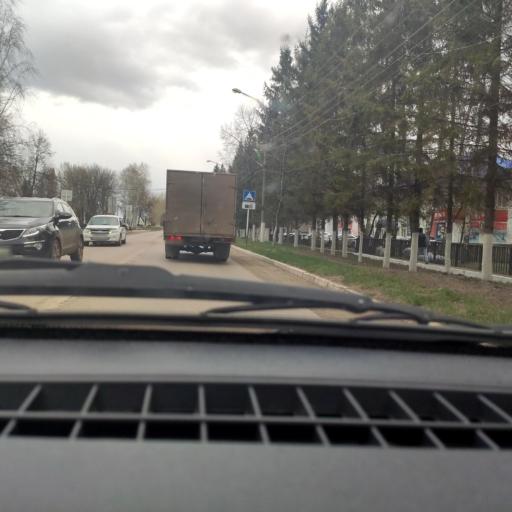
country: RU
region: Bashkortostan
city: Chekmagush
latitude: 55.1408
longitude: 54.6510
